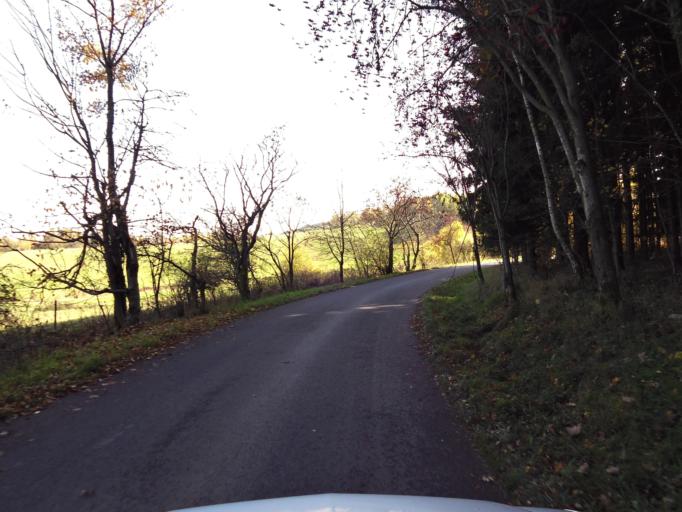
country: CZ
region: Ustecky
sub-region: Okres Chomutov
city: Perstejn
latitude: 50.4046
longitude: 13.1280
